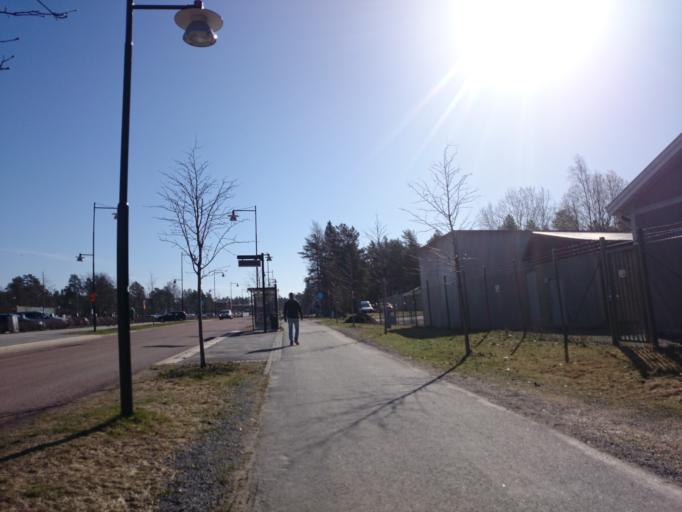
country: SE
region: Vaesterbotten
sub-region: Umea Kommun
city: Umea
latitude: 63.8178
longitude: 20.3094
